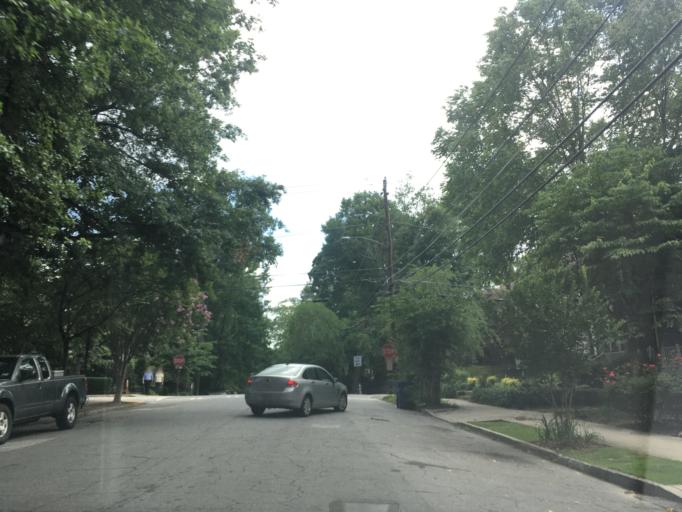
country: US
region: Georgia
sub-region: Fulton County
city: Atlanta
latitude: 33.7799
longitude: -84.3796
